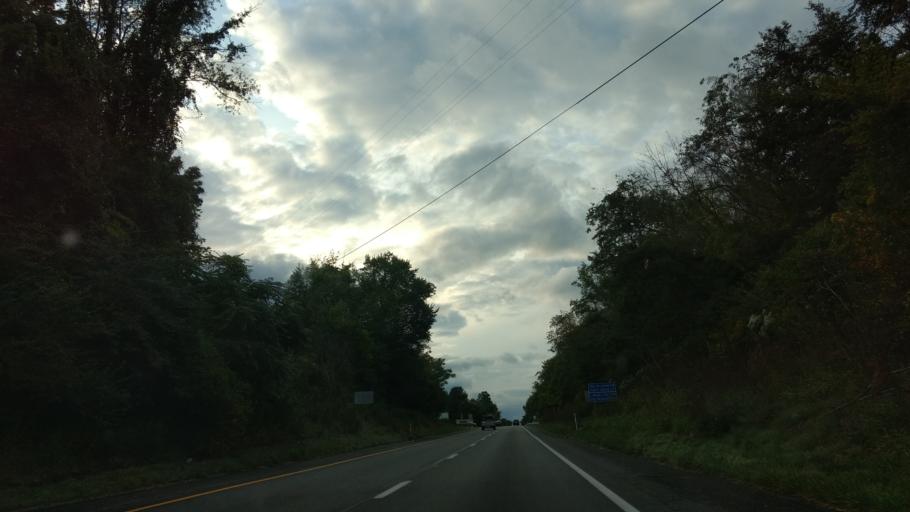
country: US
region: Pennsylvania
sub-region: Westmoreland County
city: Fellsburg
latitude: 40.1971
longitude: -79.8278
